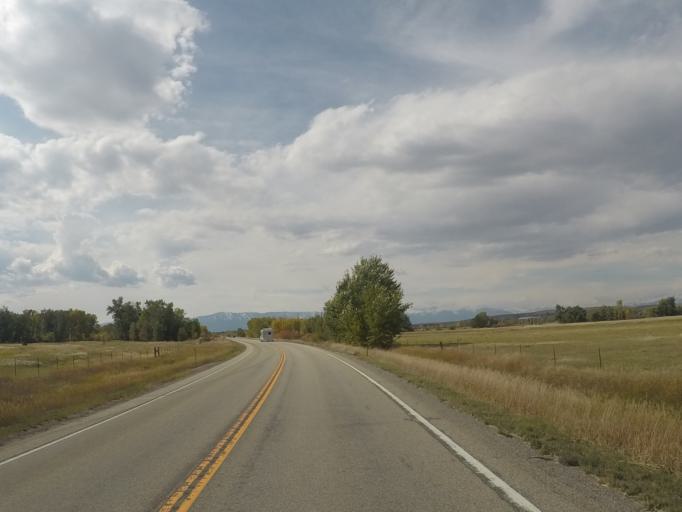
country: US
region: Montana
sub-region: Carbon County
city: Red Lodge
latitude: 45.3810
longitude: -109.1472
